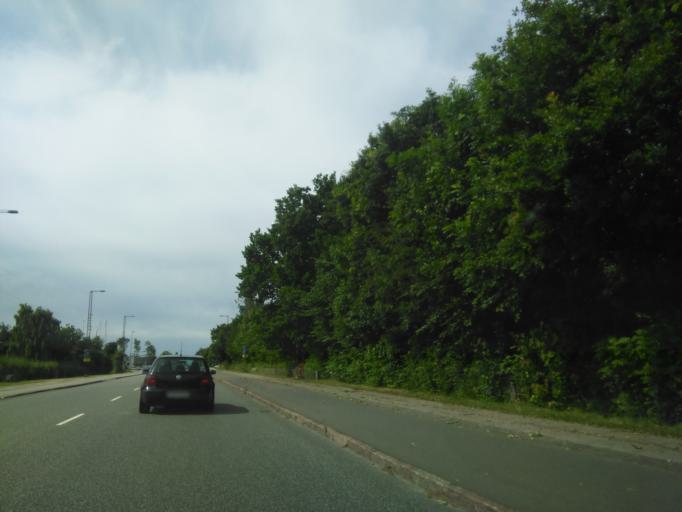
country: DK
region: Central Jutland
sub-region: Arhus Kommune
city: Stavtrup
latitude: 56.1141
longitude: 10.1590
